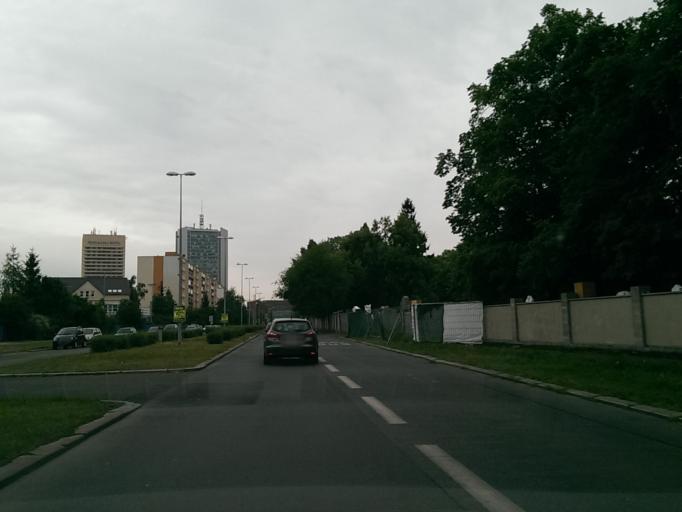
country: CZ
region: Praha
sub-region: Praha 4
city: Hodkovicky
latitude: 50.0444
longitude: 14.4392
